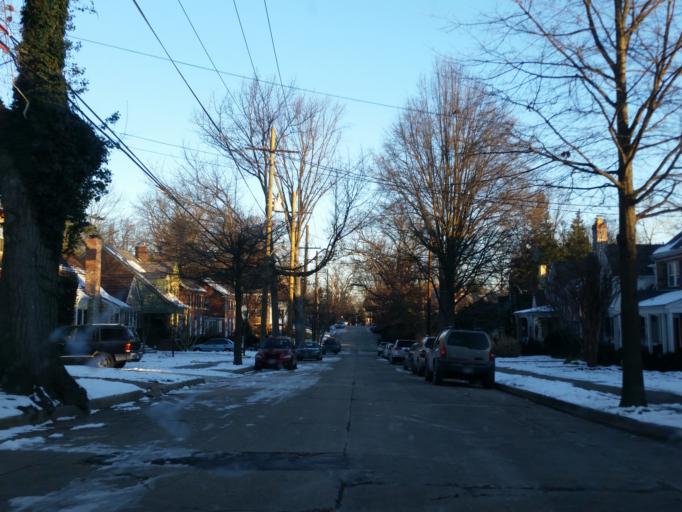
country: US
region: Maryland
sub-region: Montgomery County
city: Chevy Chase
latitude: 38.9701
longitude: -77.0639
